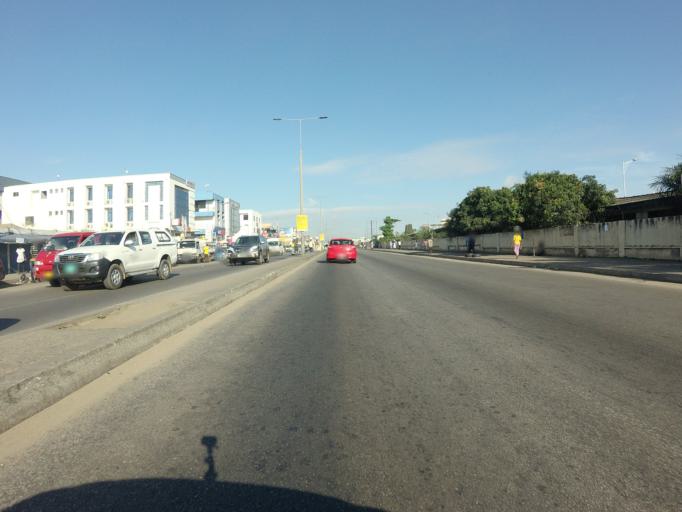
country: GH
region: Greater Accra
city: Accra
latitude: 5.5623
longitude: -0.2308
